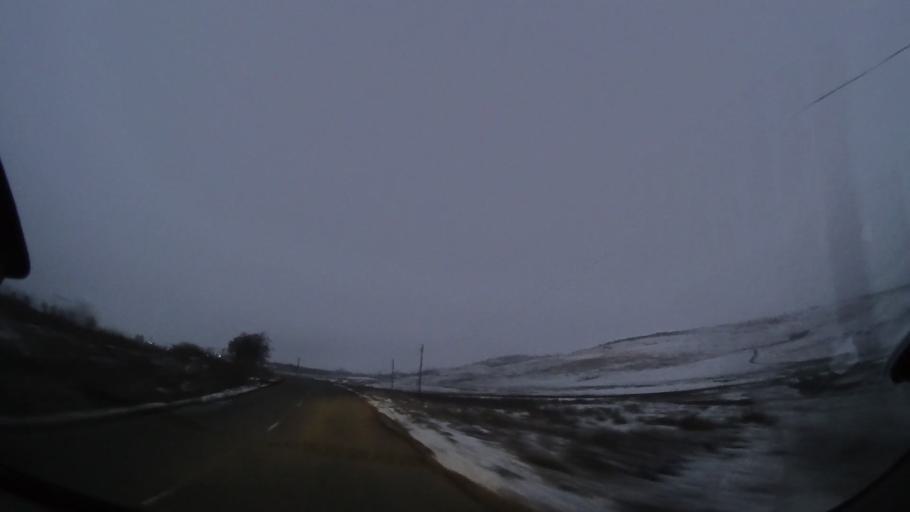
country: RO
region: Vaslui
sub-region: Comuna Dimitrie Cantemir
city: Dimitrie Cantemir
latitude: 46.4913
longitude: 28.0543
